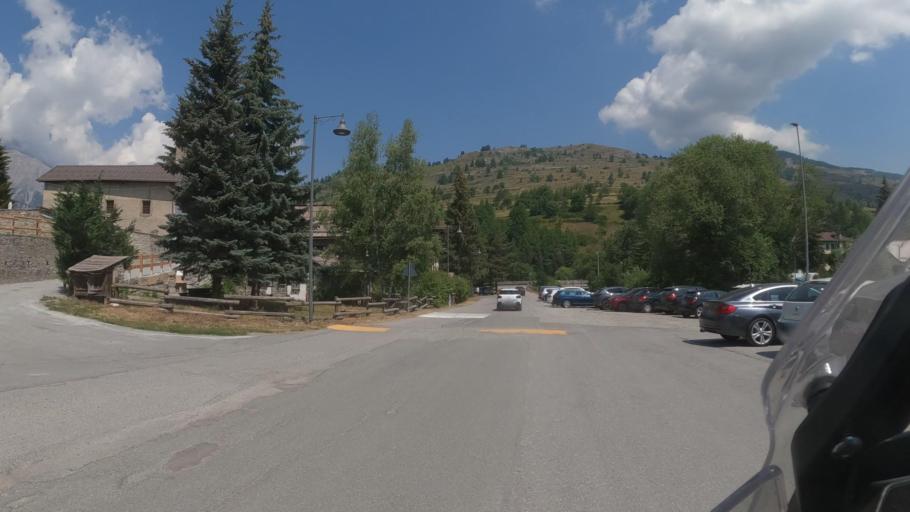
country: IT
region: Piedmont
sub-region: Provincia di Torino
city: Cesana Torinese
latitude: 44.9322
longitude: 6.8204
